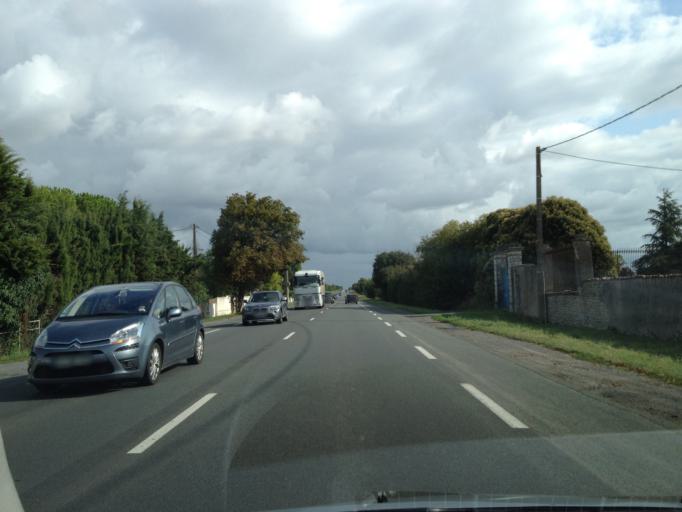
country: FR
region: Poitou-Charentes
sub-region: Departement de la Charente-Maritime
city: Sainte-Soulle
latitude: 46.2087
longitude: -1.0263
